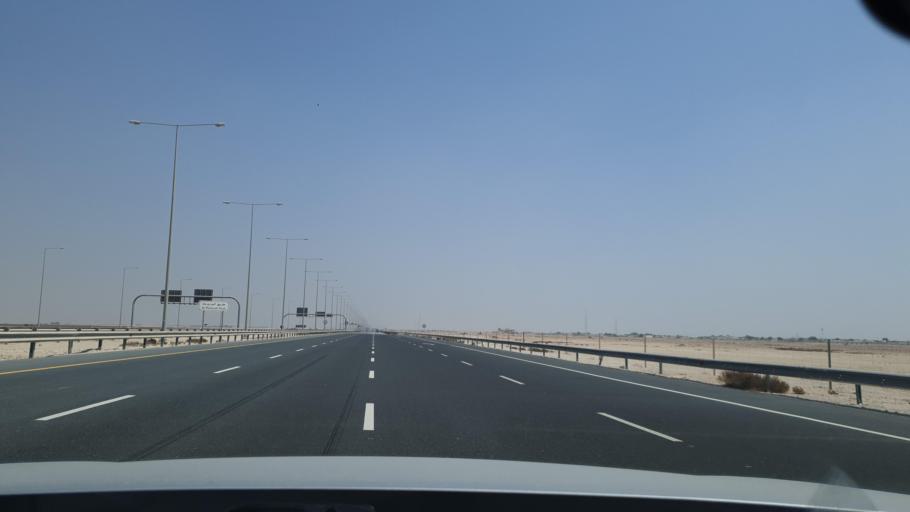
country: QA
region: Baladiyat az Za`ayin
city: Az Za`ayin
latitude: 25.6176
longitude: 51.3764
